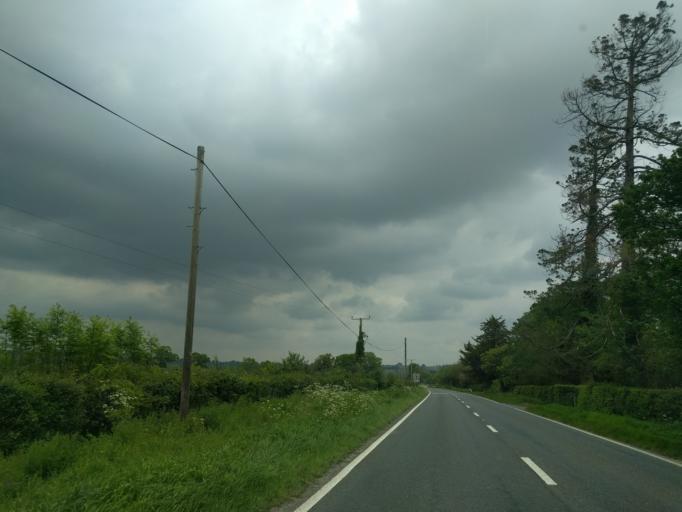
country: GB
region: England
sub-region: Somerset
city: Castle Cary
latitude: 51.1059
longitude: -2.5909
